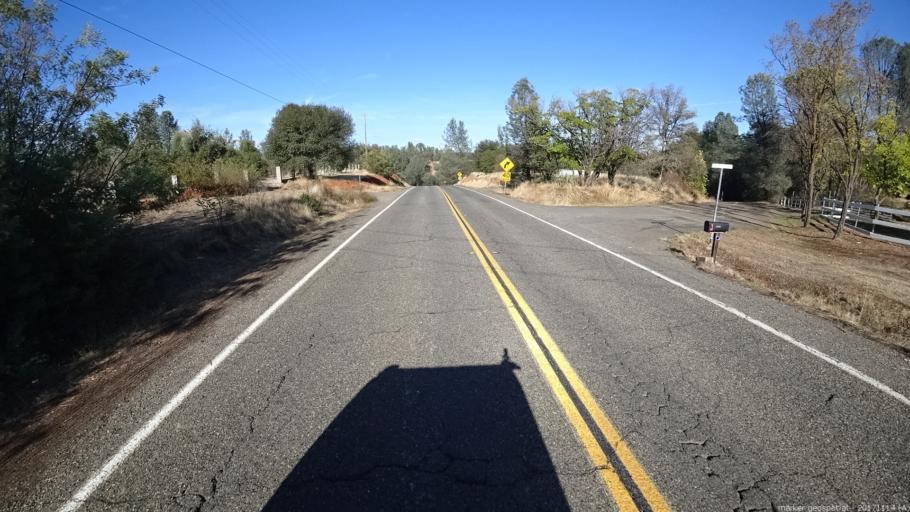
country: US
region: California
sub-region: Shasta County
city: Anderson
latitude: 40.4576
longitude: -122.4019
